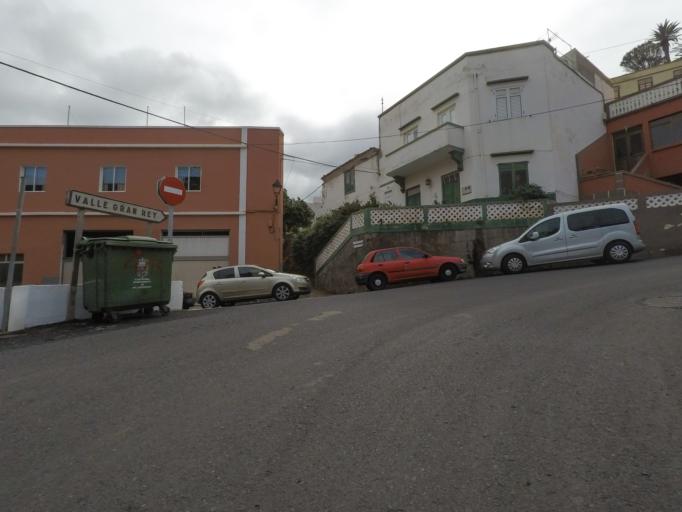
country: ES
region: Canary Islands
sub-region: Provincia de Santa Cruz de Tenerife
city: Vallehermosa
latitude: 28.1816
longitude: -17.2663
